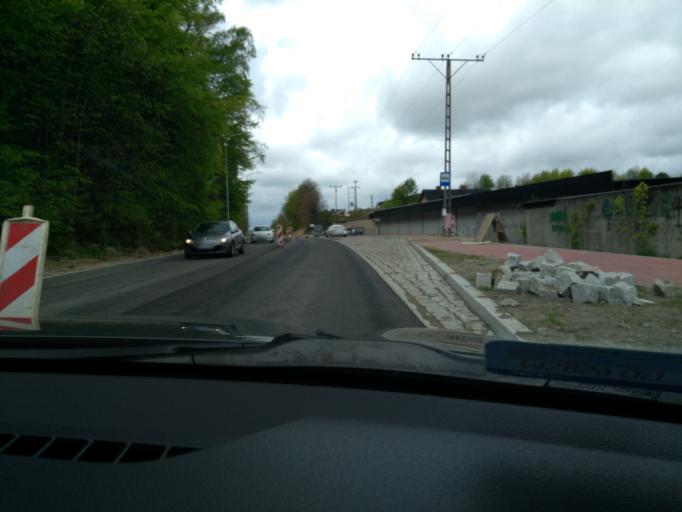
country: PL
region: Pomeranian Voivodeship
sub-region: Powiat kartuski
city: Kartuzy
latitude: 54.3446
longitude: 18.1572
